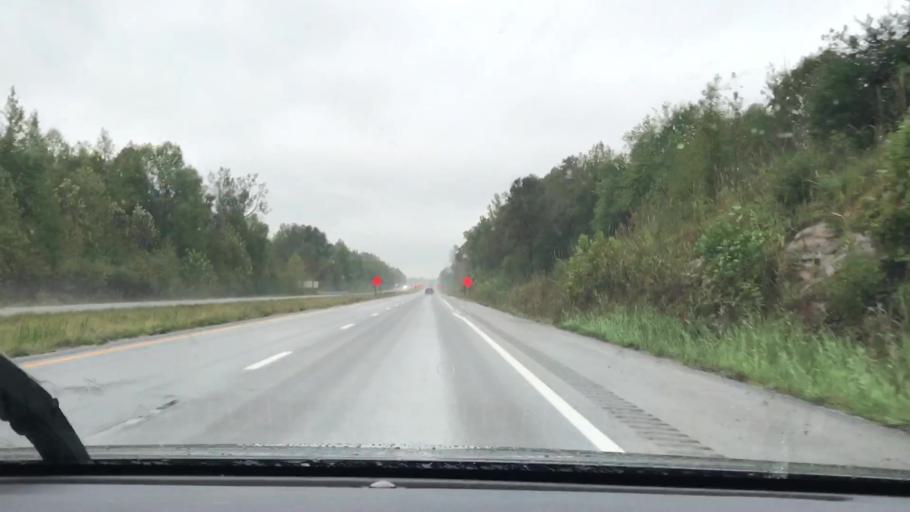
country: US
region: Kentucky
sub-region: Hopkins County
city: Nortonville
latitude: 37.1656
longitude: -87.4546
